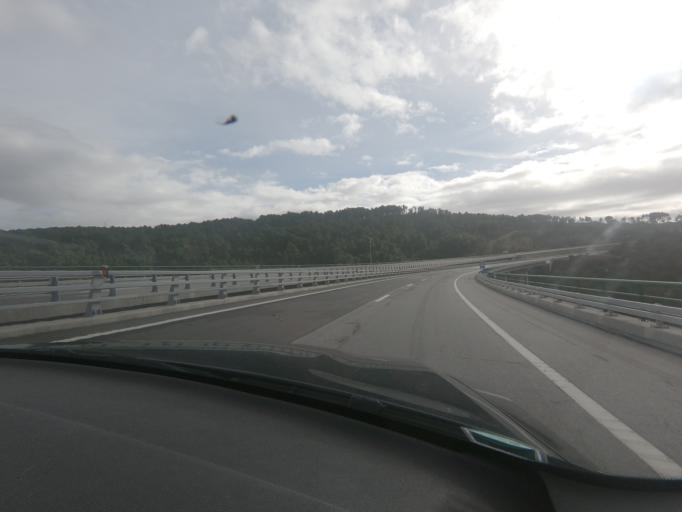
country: PT
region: Vila Real
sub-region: Vila Real
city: Vila Real
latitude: 41.3089
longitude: -7.6862
